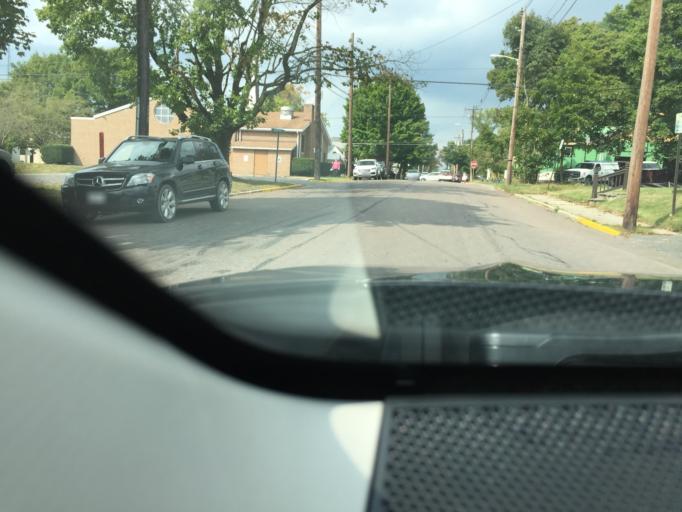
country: US
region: Maryland
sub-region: Garrett County
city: Oakland
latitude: 39.4105
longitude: -79.4059
